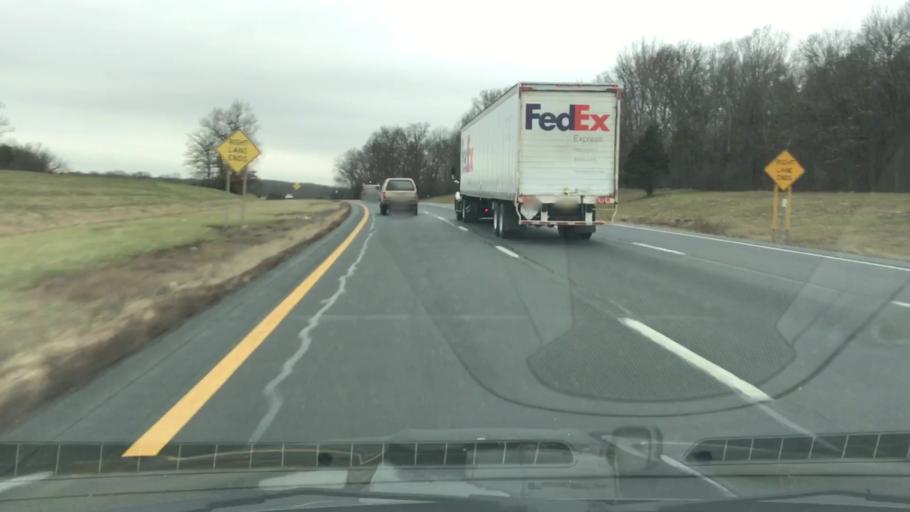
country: US
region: New York
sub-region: Orange County
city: Orange Lake
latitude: 41.5215
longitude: -74.0953
